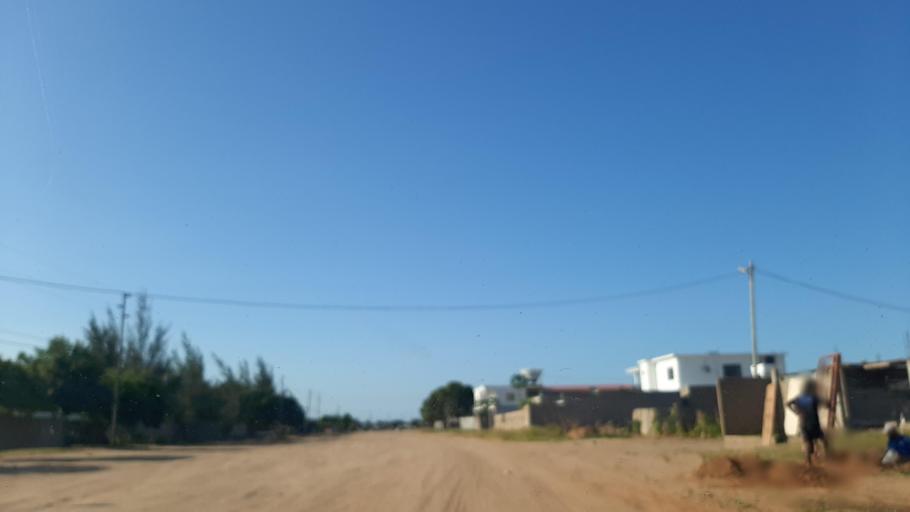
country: MZ
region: Maputo City
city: Maputo
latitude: -25.7920
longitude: 32.5522
